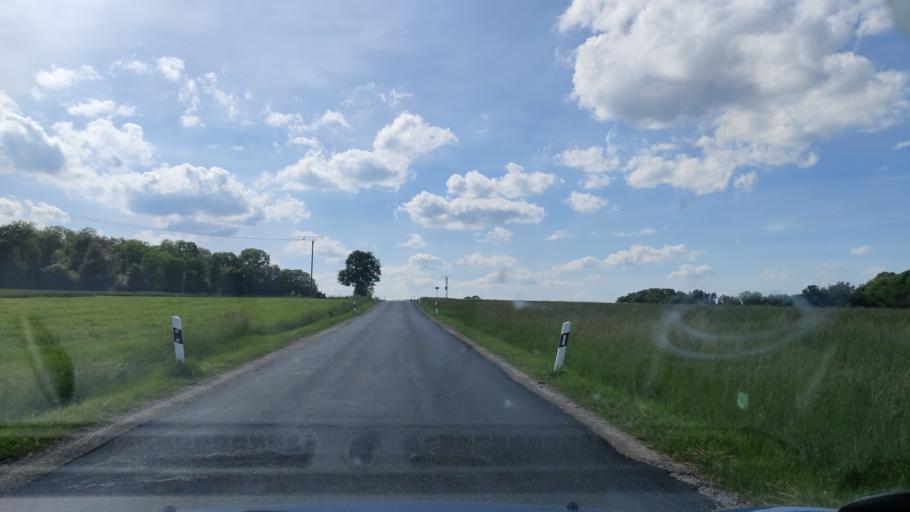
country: DE
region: Lower Saxony
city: Rosdorf
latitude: 51.5364
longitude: 9.8363
